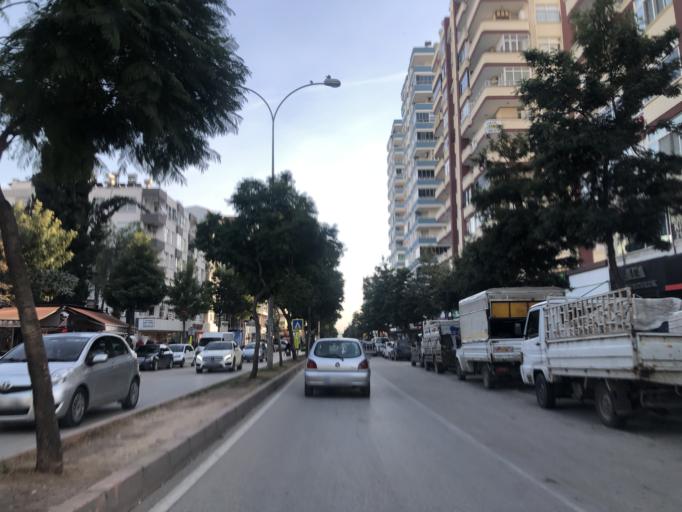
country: TR
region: Adana
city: Adana
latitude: 37.0408
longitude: 35.3039
